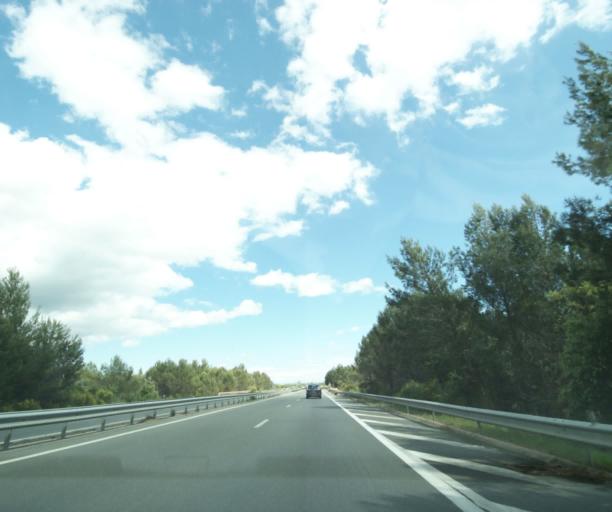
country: FR
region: Languedoc-Roussillon
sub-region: Departement de l'Herault
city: Montarnaud
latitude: 43.6296
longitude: 3.6922
